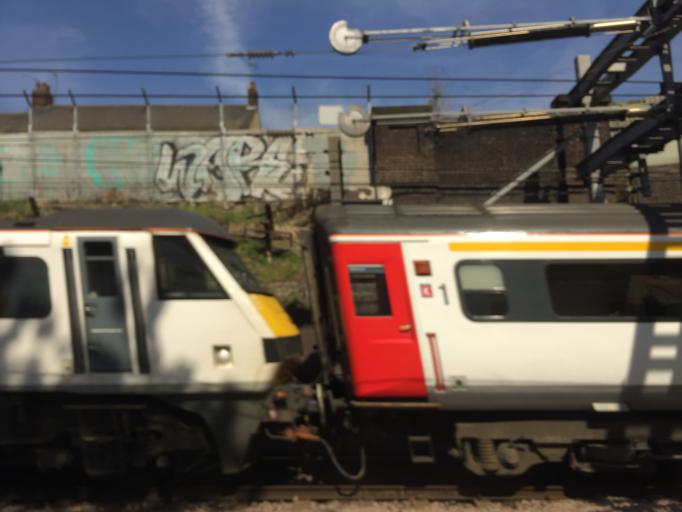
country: GB
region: England
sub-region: Greater London
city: East Ham
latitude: 51.5474
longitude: 0.0126
